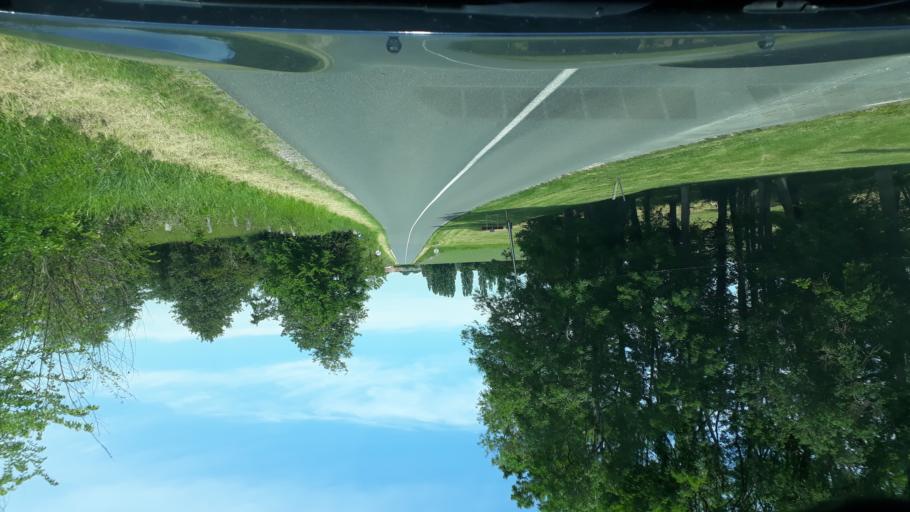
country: FR
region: Centre
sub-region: Departement du Loiret
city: Boiscommun
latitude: 48.0467
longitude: 2.3010
